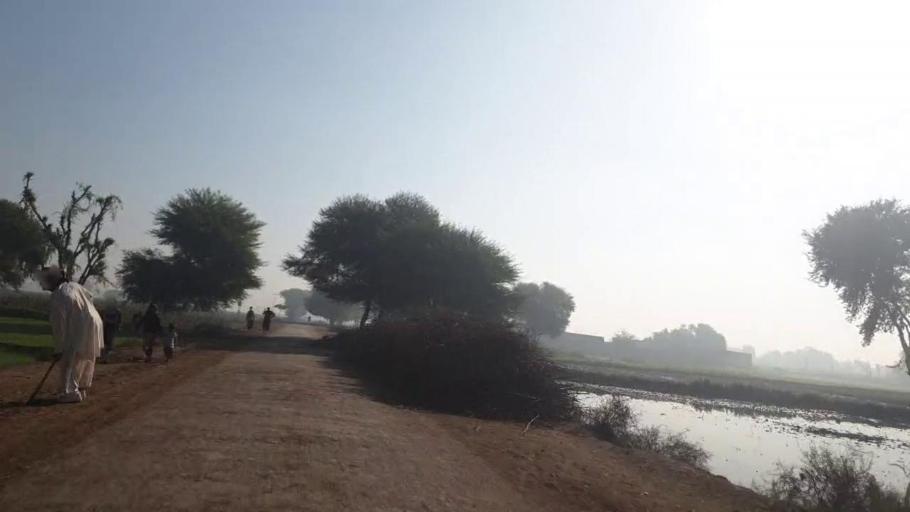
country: PK
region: Sindh
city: Dadu
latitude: 26.6754
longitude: 67.7900
